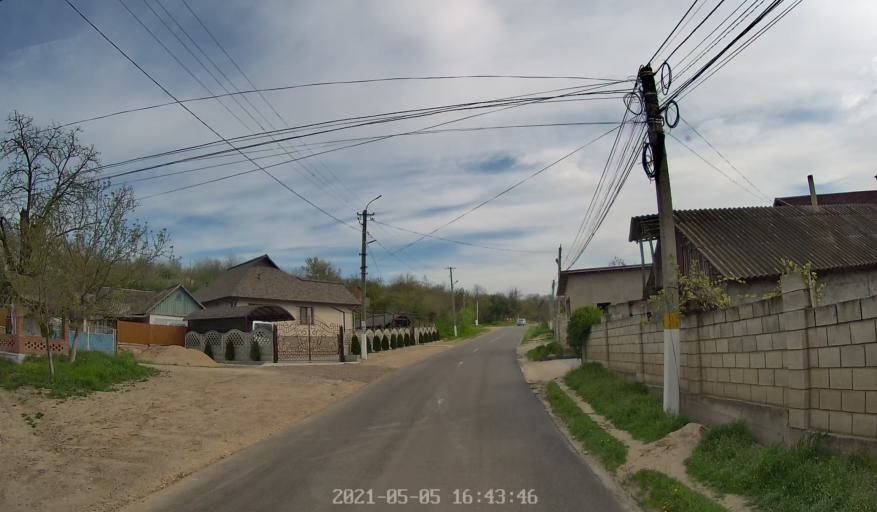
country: MD
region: Criuleni
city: Criuleni
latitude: 47.1219
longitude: 29.1943
